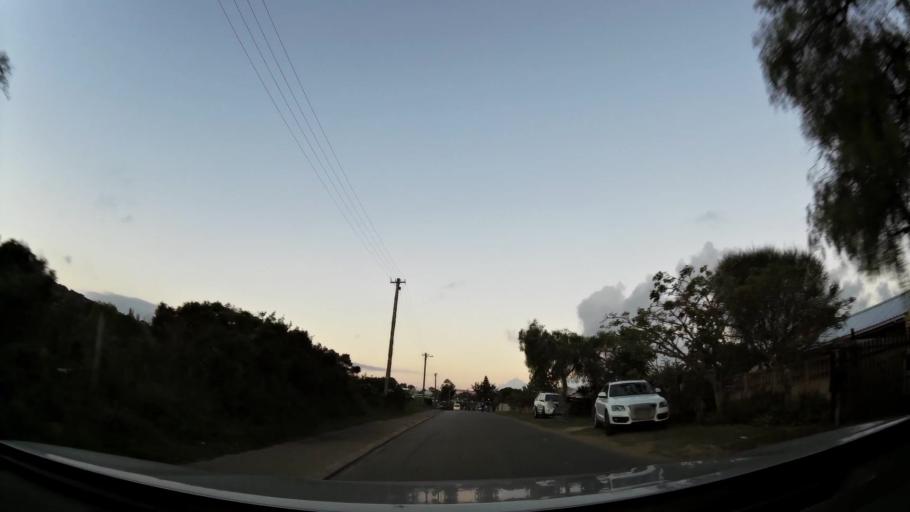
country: ZA
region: Western Cape
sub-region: Eden District Municipality
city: Knysna
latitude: -34.0266
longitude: 22.8106
